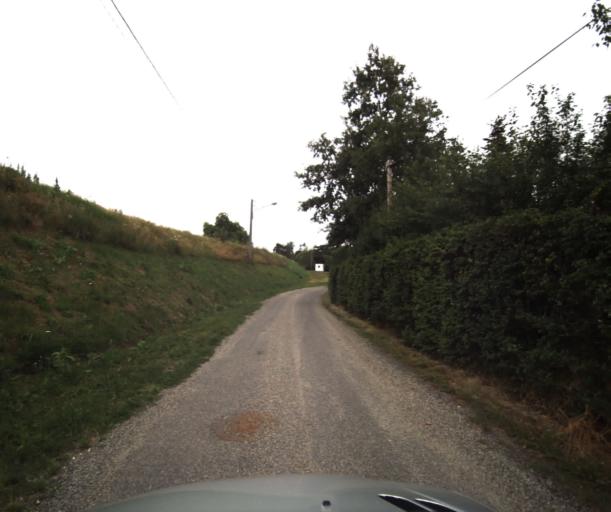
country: FR
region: Midi-Pyrenees
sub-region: Departement de la Haute-Garonne
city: Pinsaguel
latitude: 43.5065
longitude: 1.3858
